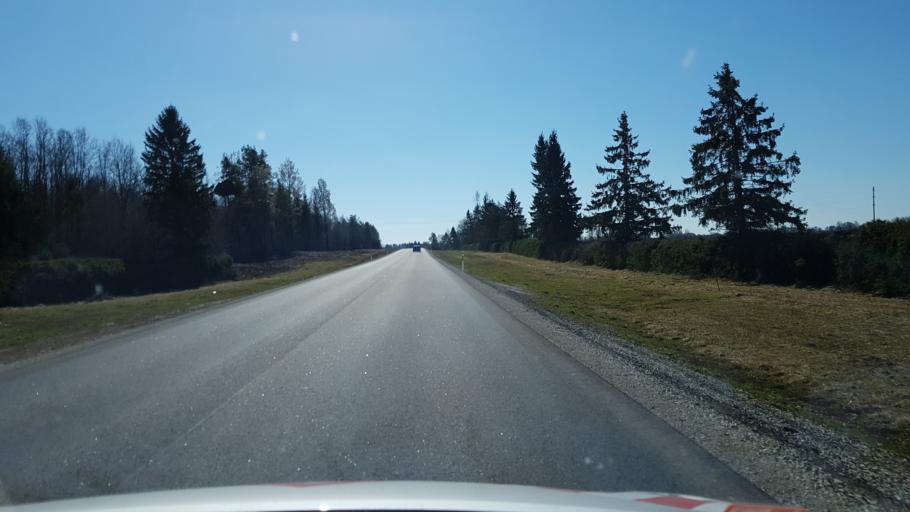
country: EE
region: Laeaene-Virumaa
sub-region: Vinni vald
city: Vinni
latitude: 59.0843
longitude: 26.6272
